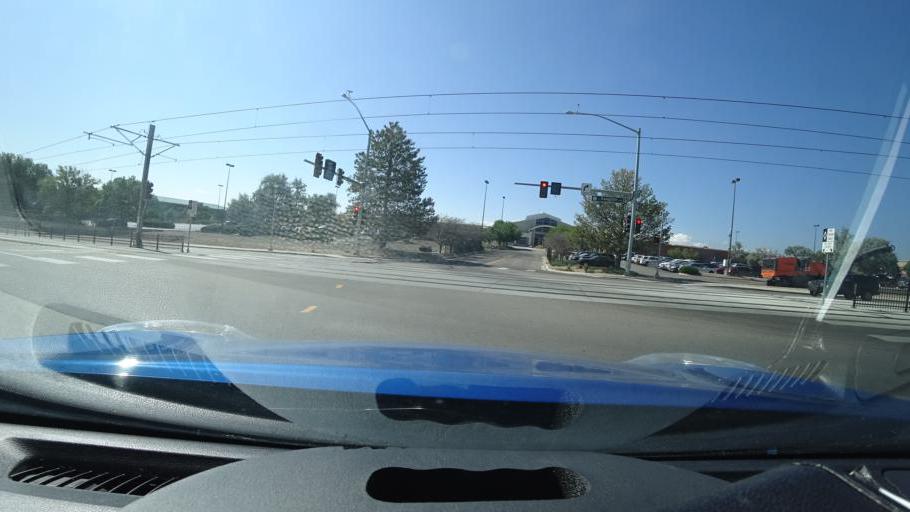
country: US
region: Colorado
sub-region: Adams County
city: Aurora
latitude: 39.7041
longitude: -104.8233
